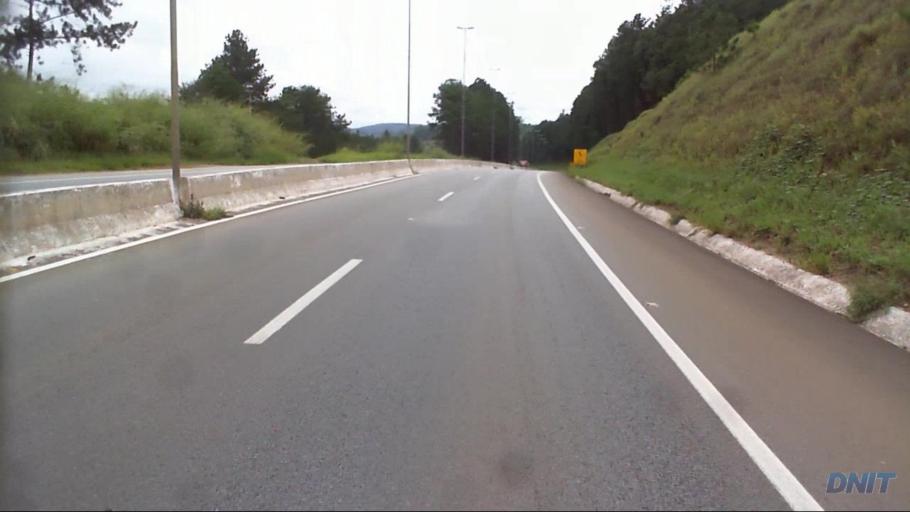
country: BR
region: Minas Gerais
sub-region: Nova Era
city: Nova Era
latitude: -19.7676
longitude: -43.0471
